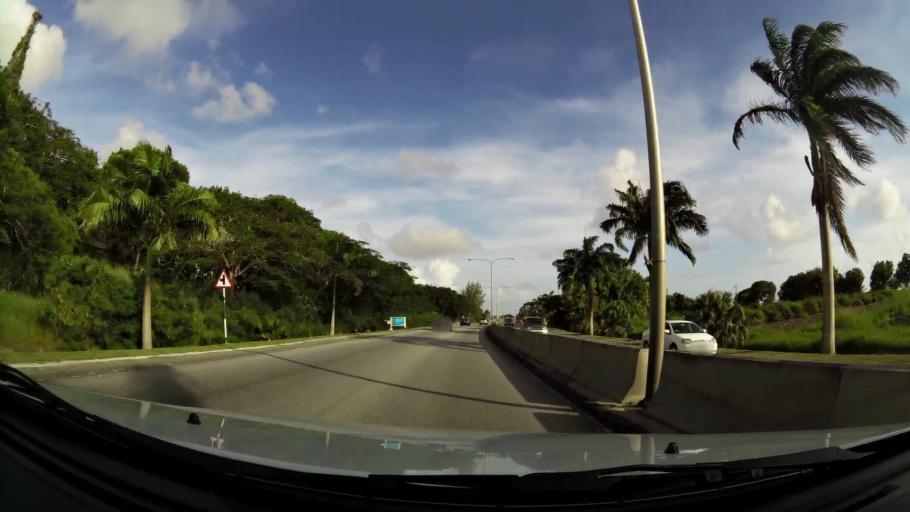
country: BB
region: Christ Church
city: Oistins
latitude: 13.0794
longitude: -59.5716
